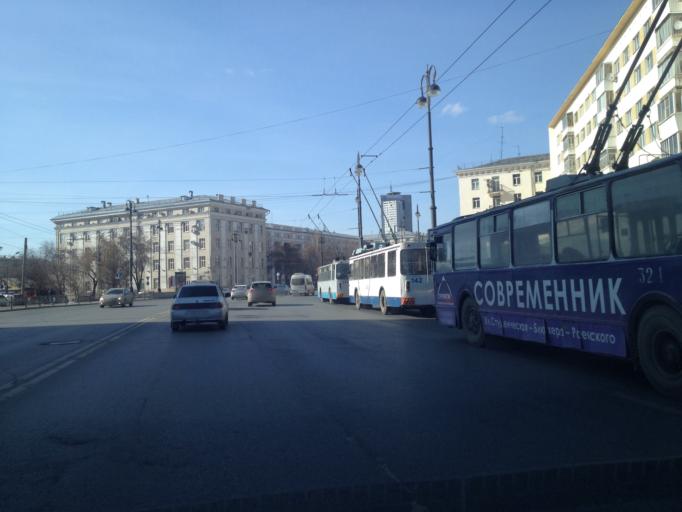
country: RU
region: Sverdlovsk
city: Yekaterinburg
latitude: 56.8493
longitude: 60.6070
